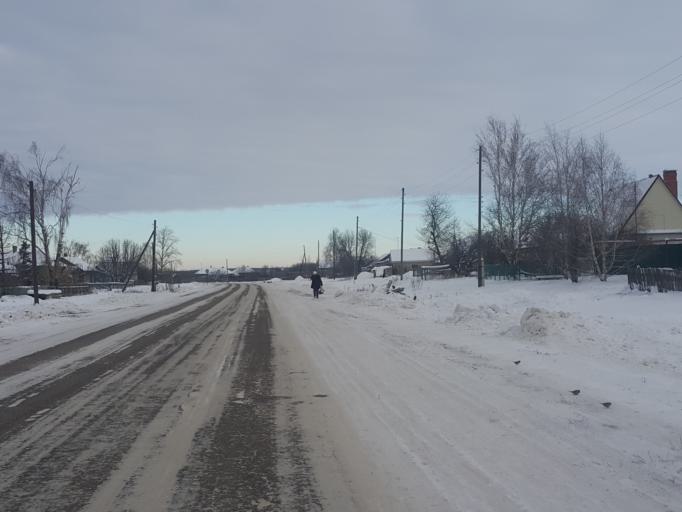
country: RU
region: Tambov
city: Platonovka
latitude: 52.8352
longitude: 41.8119
